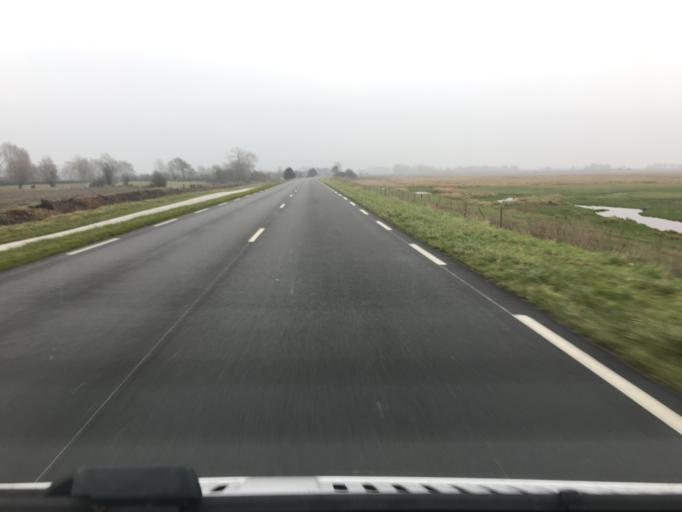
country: FR
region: Picardie
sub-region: Departement de la Somme
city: Saint-Valery-sur-Somme
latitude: 50.2072
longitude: 1.6807
